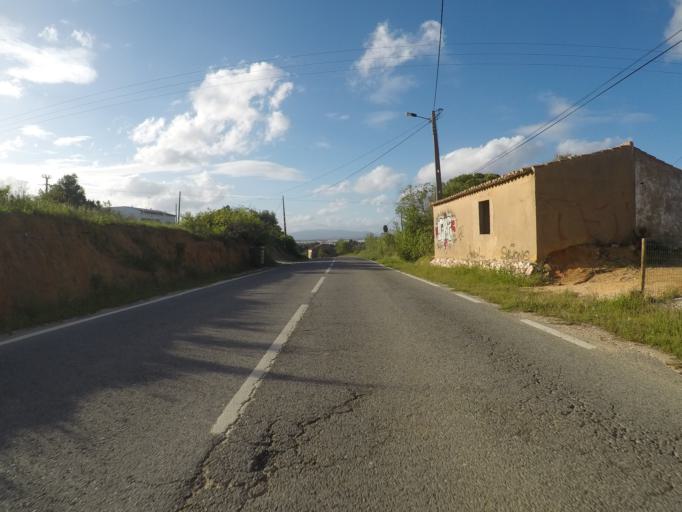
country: PT
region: Faro
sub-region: Lagoa
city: Carvoeiro
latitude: 37.1033
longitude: -8.4444
